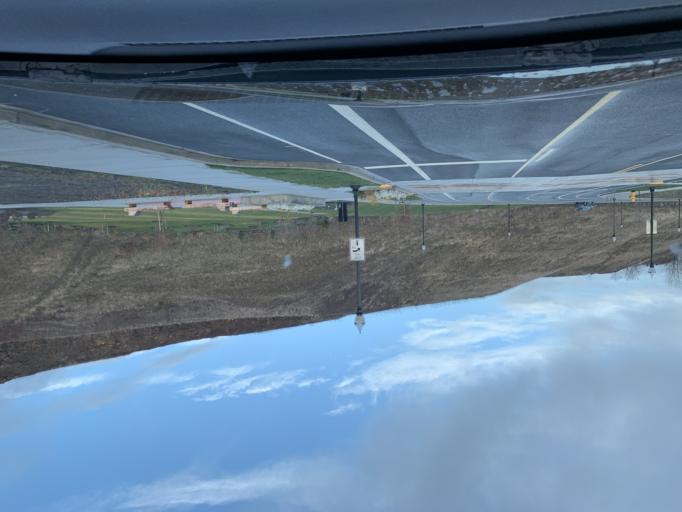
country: US
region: Washington
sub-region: Clark County
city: Mill Plain
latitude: 45.5886
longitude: -122.4705
